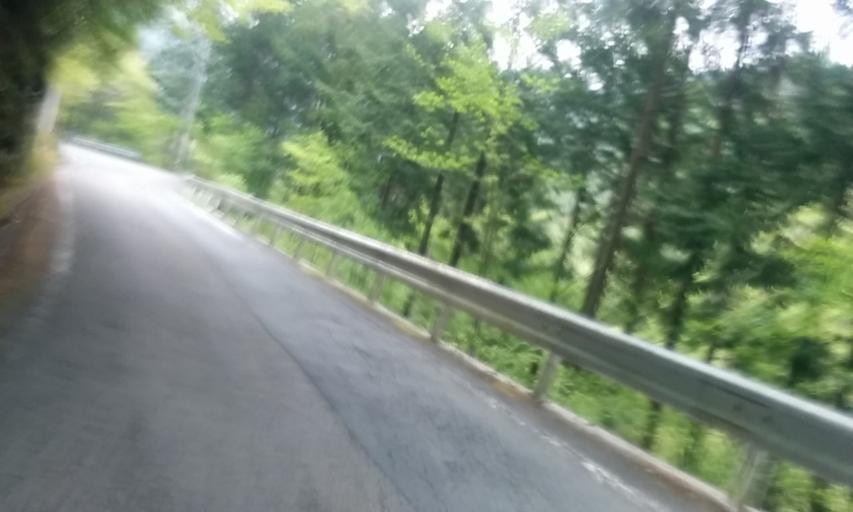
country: JP
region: Ehime
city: Saijo
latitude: 33.8000
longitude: 133.2810
